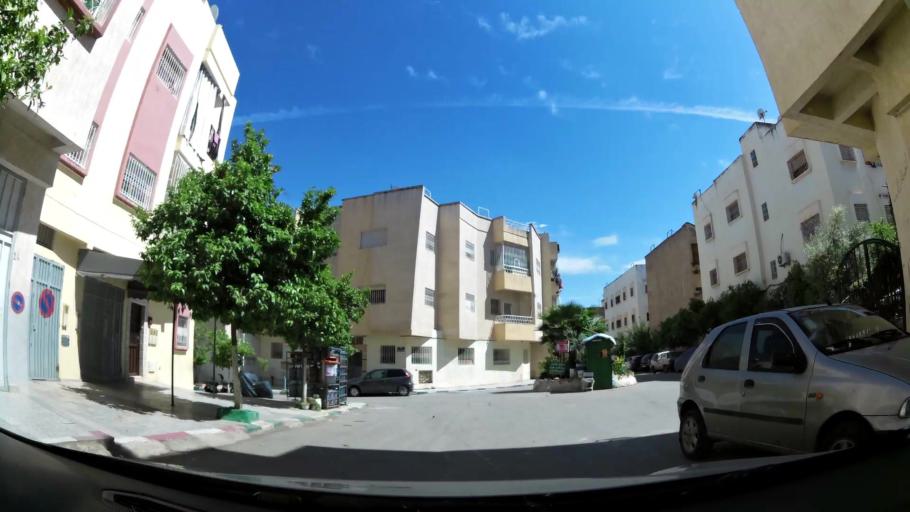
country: MA
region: Fes-Boulemane
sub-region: Fes
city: Fes
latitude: 34.0030
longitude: -4.9858
